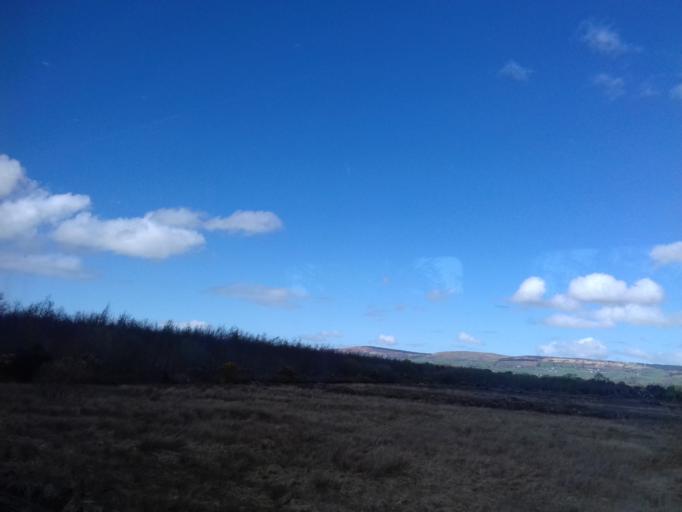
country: IE
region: Munster
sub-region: Ciarrai
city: Tralee
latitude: 52.2378
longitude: -9.5993
